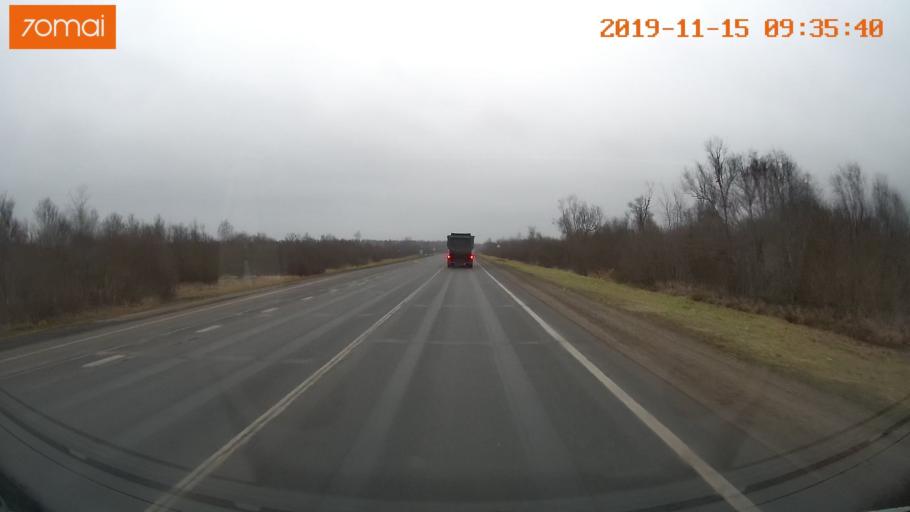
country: RU
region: Vologda
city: Sheksna
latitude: 59.2529
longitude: 38.4045
